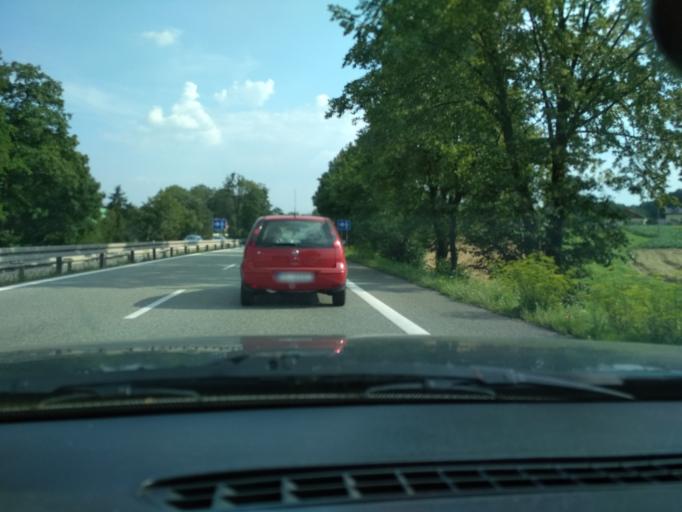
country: PL
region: Silesian Voivodeship
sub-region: Powiat pszczynski
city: Pawlowice
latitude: 49.9994
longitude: 18.7113
